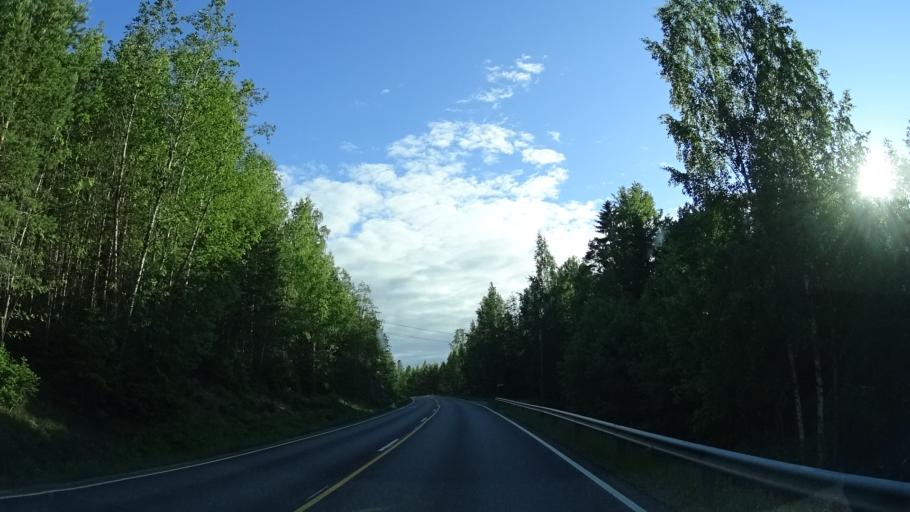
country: FI
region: Paijanne Tavastia
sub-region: Lahti
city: Asikkala
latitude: 61.3373
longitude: 25.5823
